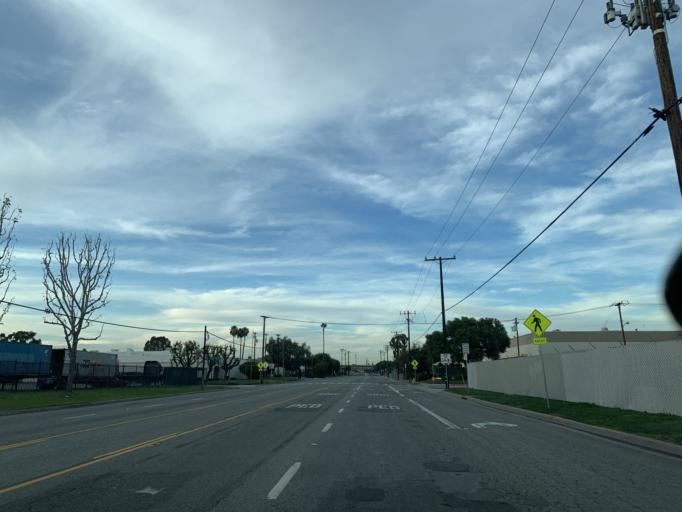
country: US
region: California
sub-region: Los Angeles County
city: Compton
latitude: 33.8686
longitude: -118.2129
